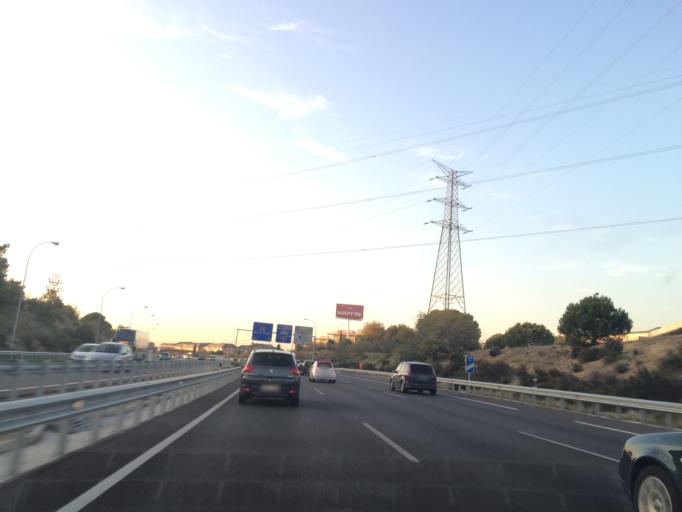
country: ES
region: Madrid
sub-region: Provincia de Madrid
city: Majadahonda
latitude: 40.4464
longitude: -3.8538
